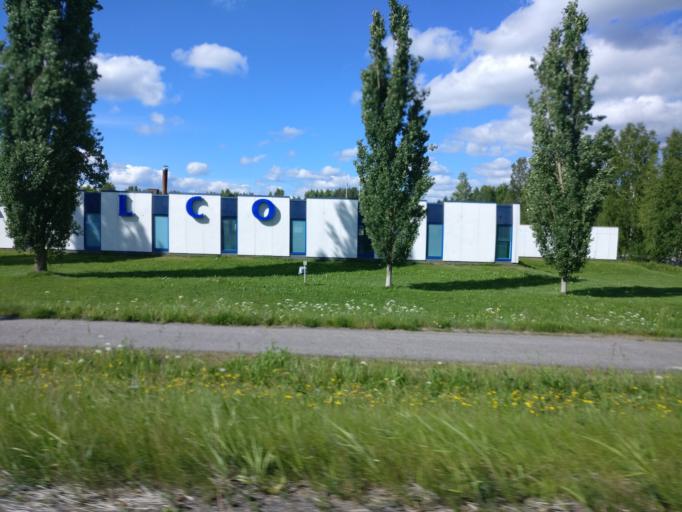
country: FI
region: Southern Savonia
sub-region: Savonlinna
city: Savonlinna
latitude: 61.8774
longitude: 28.9798
